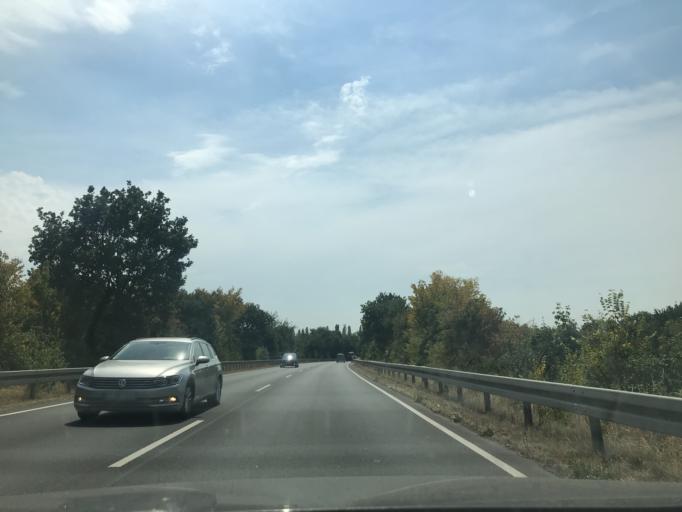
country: DE
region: North Rhine-Westphalia
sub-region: Regierungsbezirk Dusseldorf
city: Alpen
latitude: 51.5771
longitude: 6.5265
